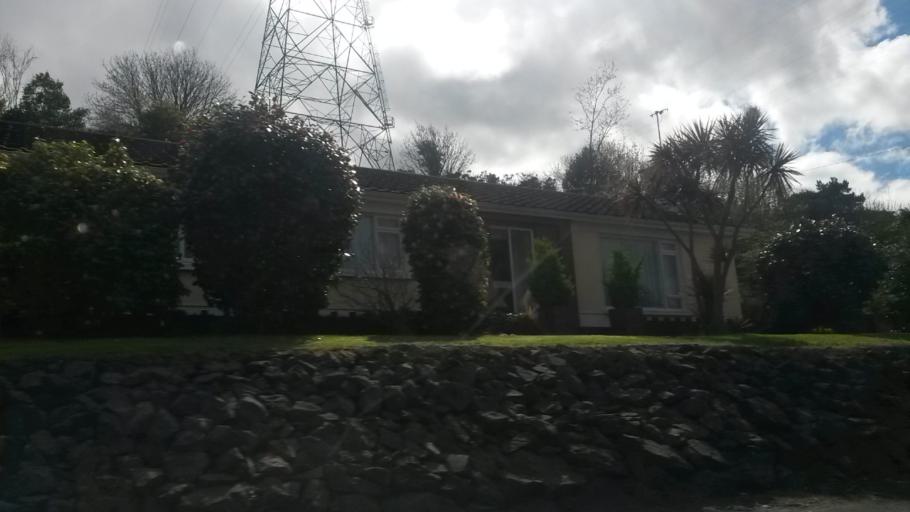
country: IE
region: Munster
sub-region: County Cork
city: Passage West
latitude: 51.8543
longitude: -8.3272
